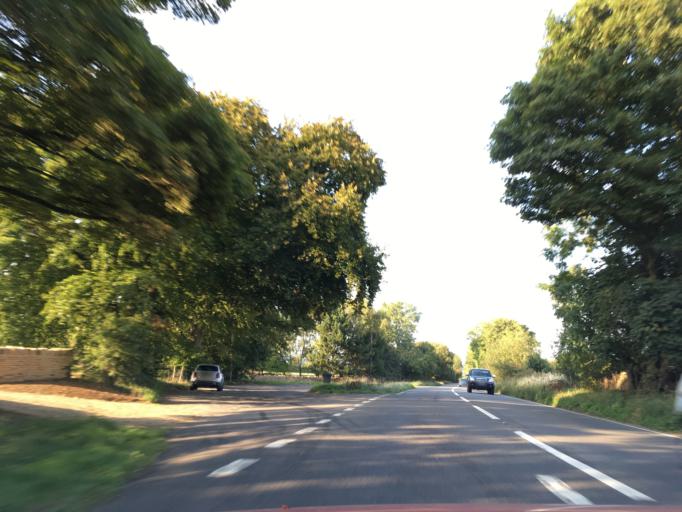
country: GB
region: England
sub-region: Gloucestershire
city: Stow on the Wold
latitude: 51.9387
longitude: -1.7222
